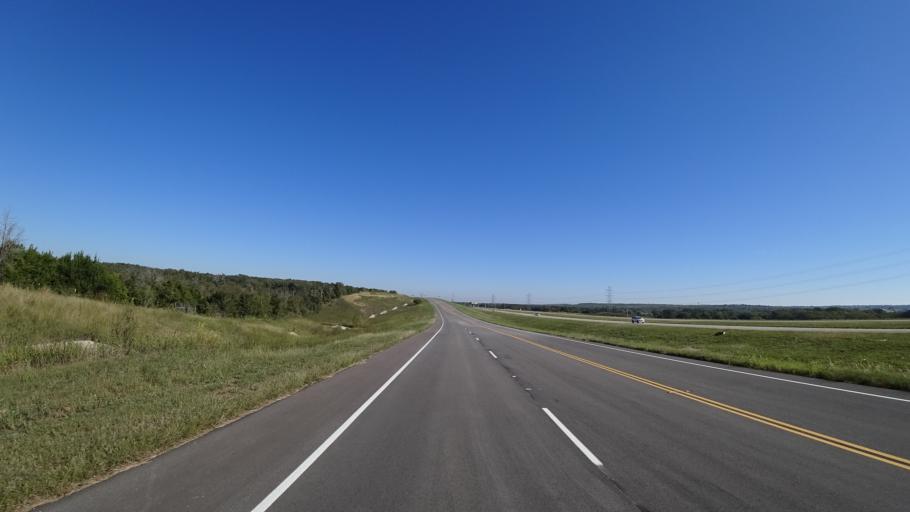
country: US
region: Texas
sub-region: Travis County
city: Manor
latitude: 30.2949
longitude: -97.5721
